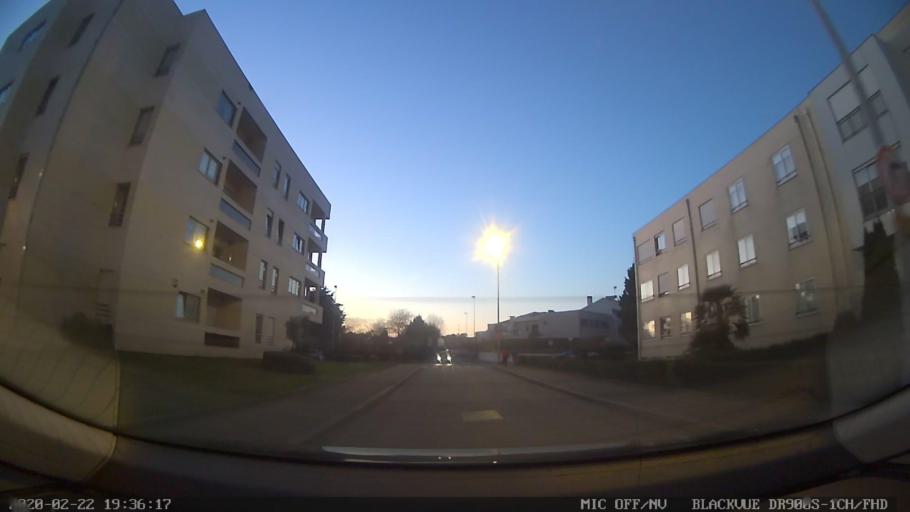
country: PT
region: Porto
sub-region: Matosinhos
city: Senhora da Hora
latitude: 41.1860
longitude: -8.6362
